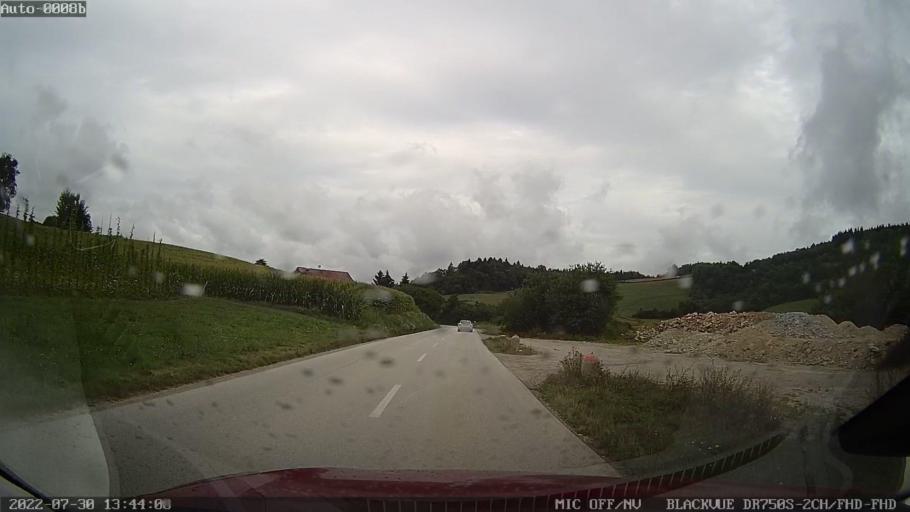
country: SI
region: Ivancna Gorica
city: Sentvid pri Sticni
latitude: 45.9153
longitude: 14.8913
